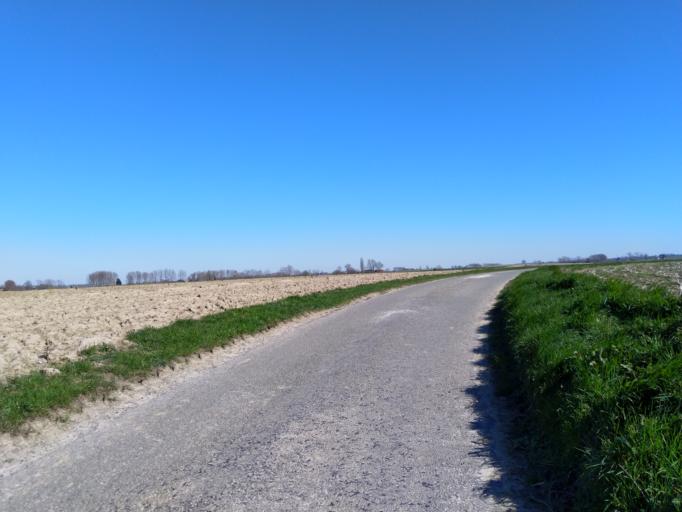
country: BE
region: Wallonia
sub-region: Province du Hainaut
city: Jurbise
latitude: 50.5525
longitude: 3.9284
